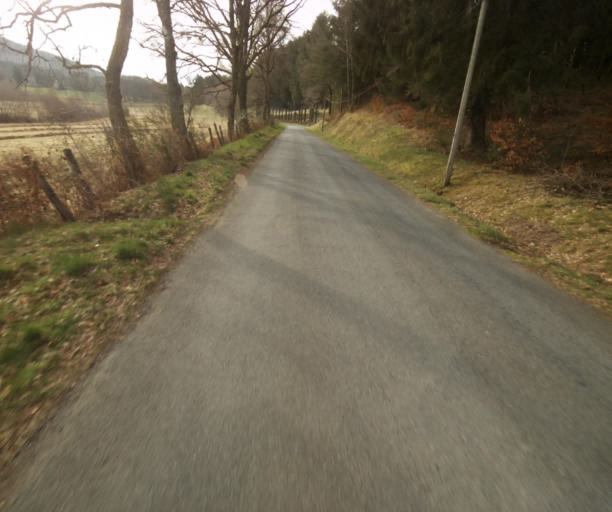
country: FR
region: Limousin
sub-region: Departement de la Correze
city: Treignac
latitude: 45.4688
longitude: 1.8049
